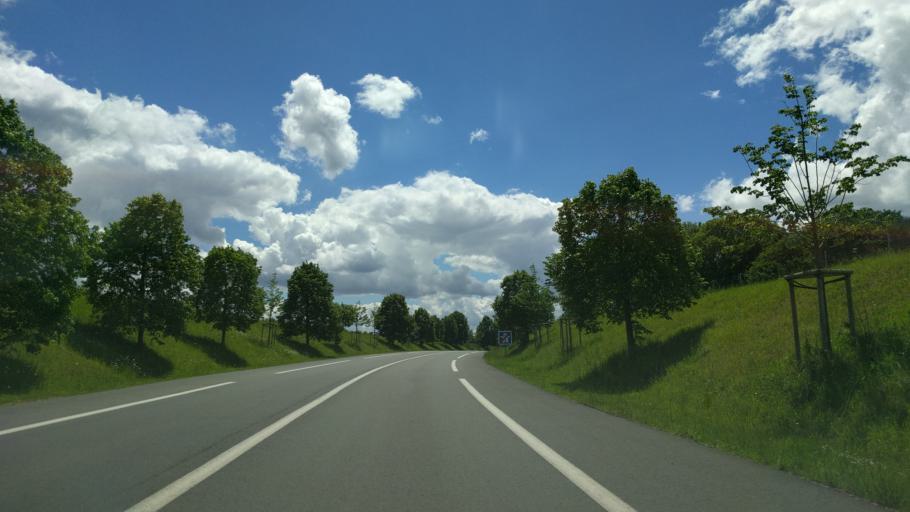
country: FR
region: Picardie
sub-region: Departement de la Somme
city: Peronne
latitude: 49.9638
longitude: 2.8633
